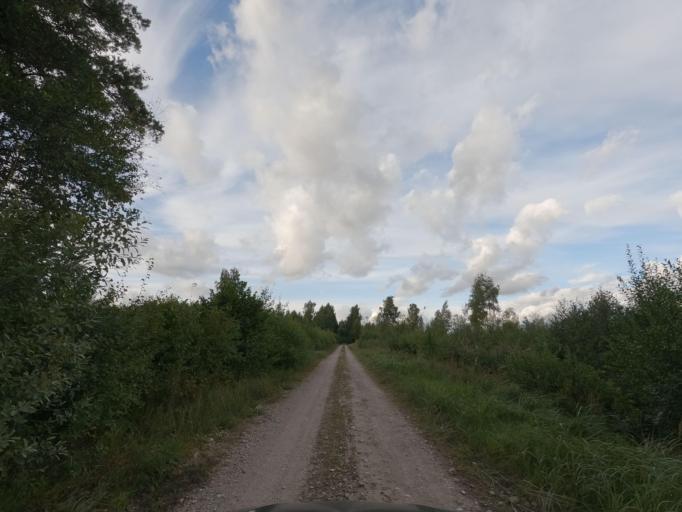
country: EE
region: Raplamaa
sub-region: Rapla vald
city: Rapla
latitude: 59.0105
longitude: 24.7606
